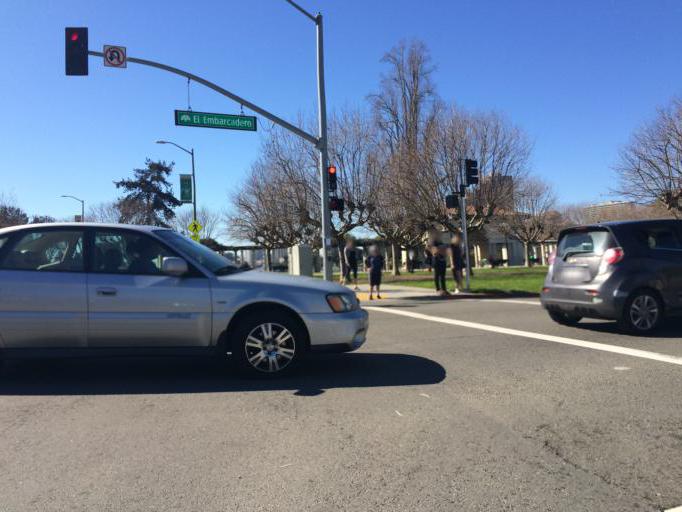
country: US
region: California
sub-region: Alameda County
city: Oakland
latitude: 37.8087
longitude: -122.2488
